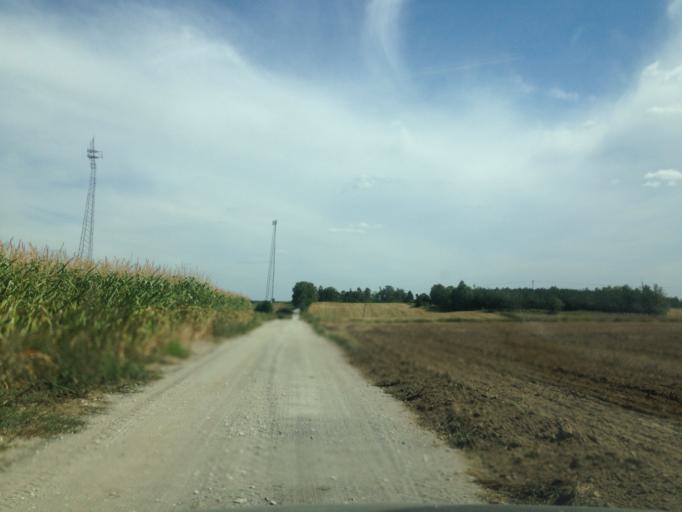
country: PL
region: Kujawsko-Pomorskie
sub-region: Powiat brodnicki
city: Gorzno
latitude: 53.2016
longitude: 19.6295
